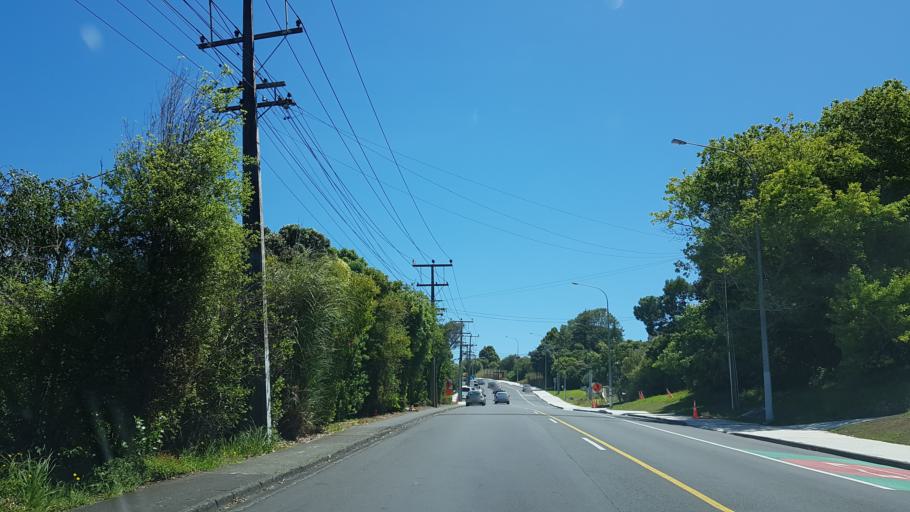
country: NZ
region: Auckland
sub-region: Auckland
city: North Shore
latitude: -36.8054
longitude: 174.7443
